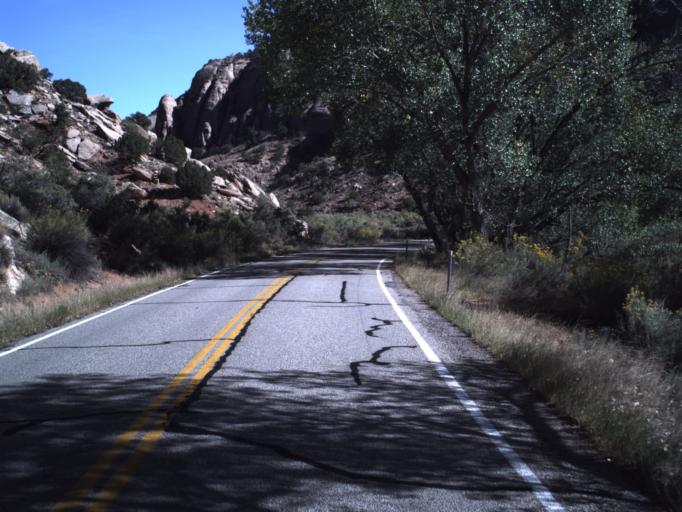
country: US
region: Utah
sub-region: San Juan County
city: Monticello
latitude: 38.0267
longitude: -109.5403
